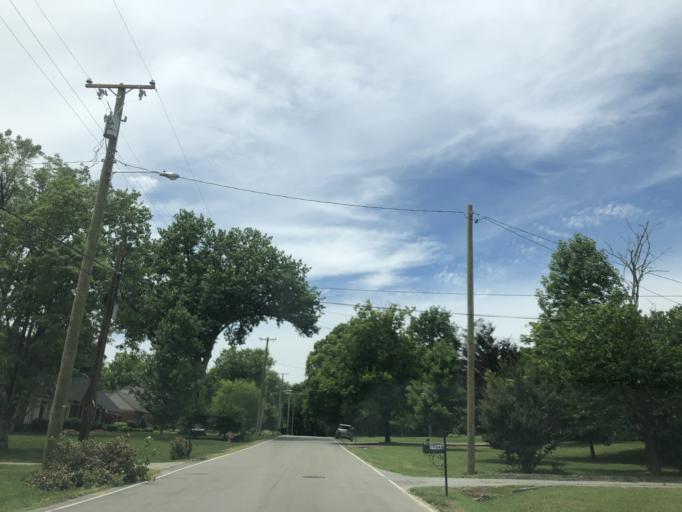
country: US
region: Tennessee
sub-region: Davidson County
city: Oak Hill
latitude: 36.1116
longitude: -86.7979
